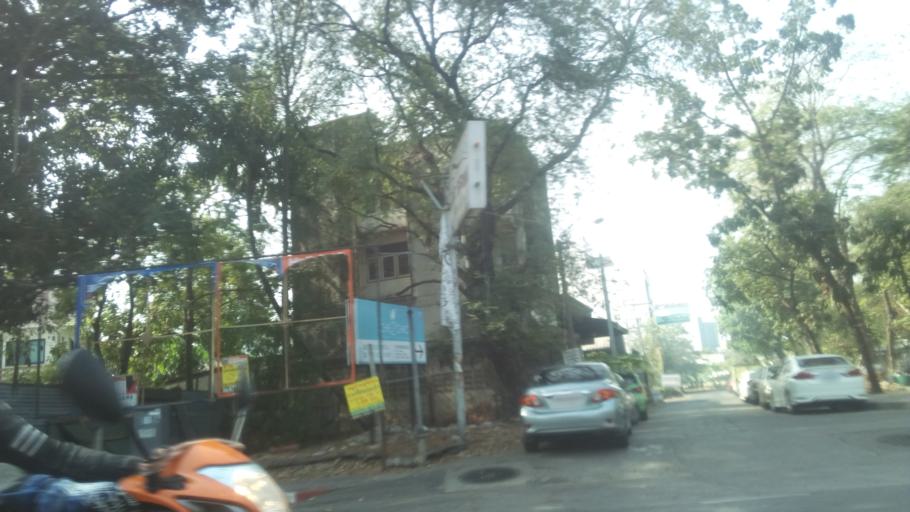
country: TH
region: Bangkok
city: Chatuchak
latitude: 13.8398
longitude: 100.5430
